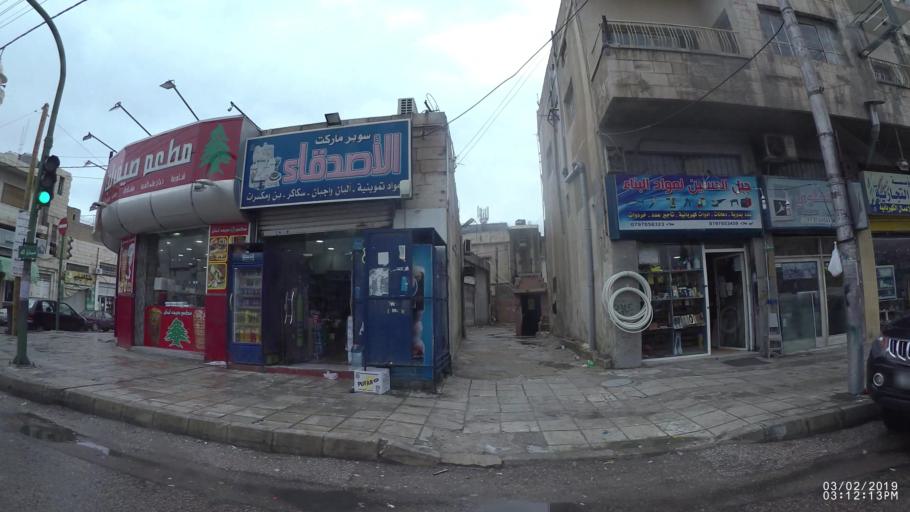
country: JO
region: Amman
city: Amman
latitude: 31.9608
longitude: 35.9286
